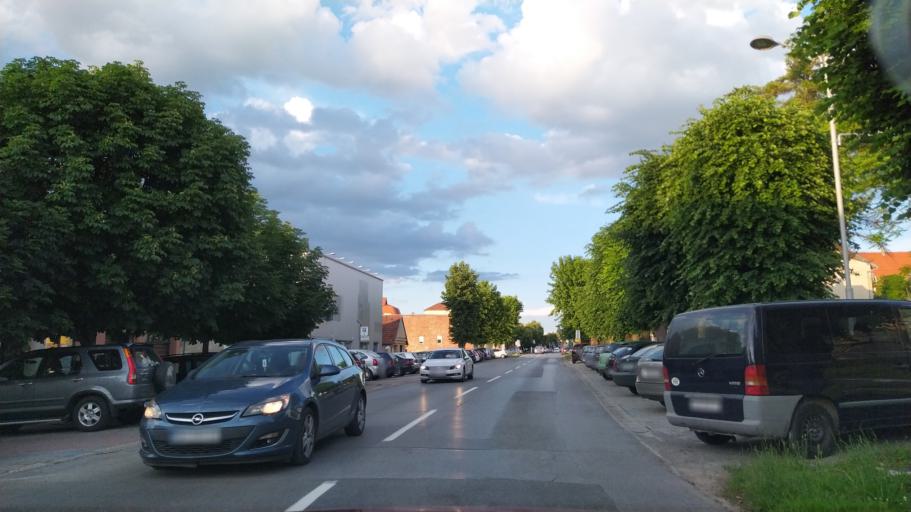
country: HR
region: Osjecko-Baranjska
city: Nasice
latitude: 45.4896
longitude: 18.0875
